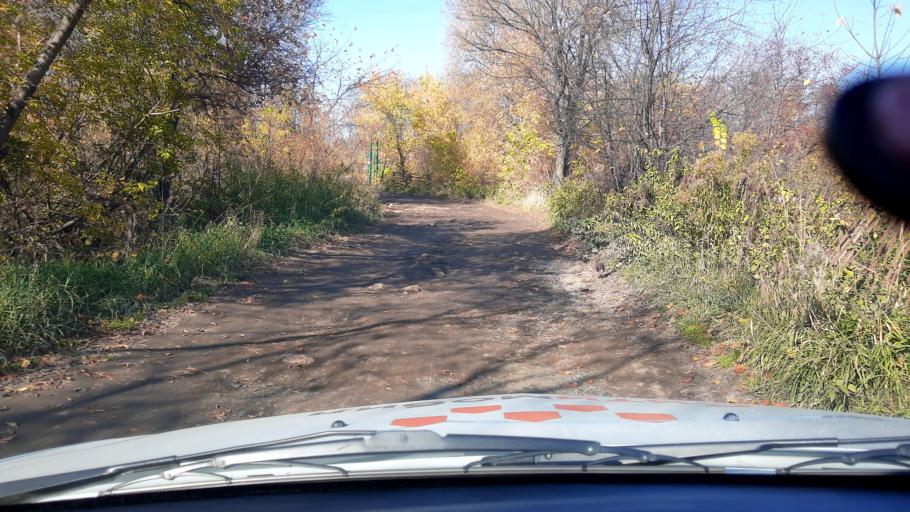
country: RU
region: Bashkortostan
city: Ufa
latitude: 54.8627
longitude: 56.1328
